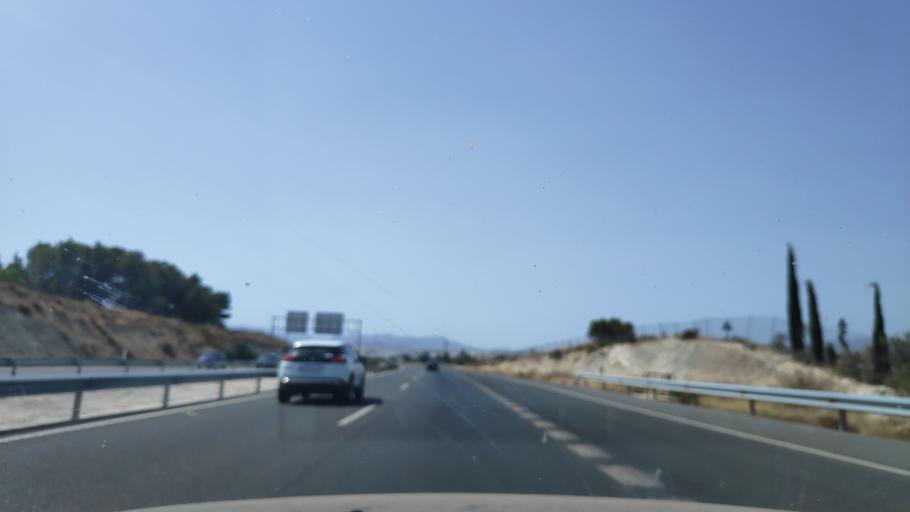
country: ES
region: Murcia
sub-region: Murcia
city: Molina de Segura
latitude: 38.0750
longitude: -1.2055
